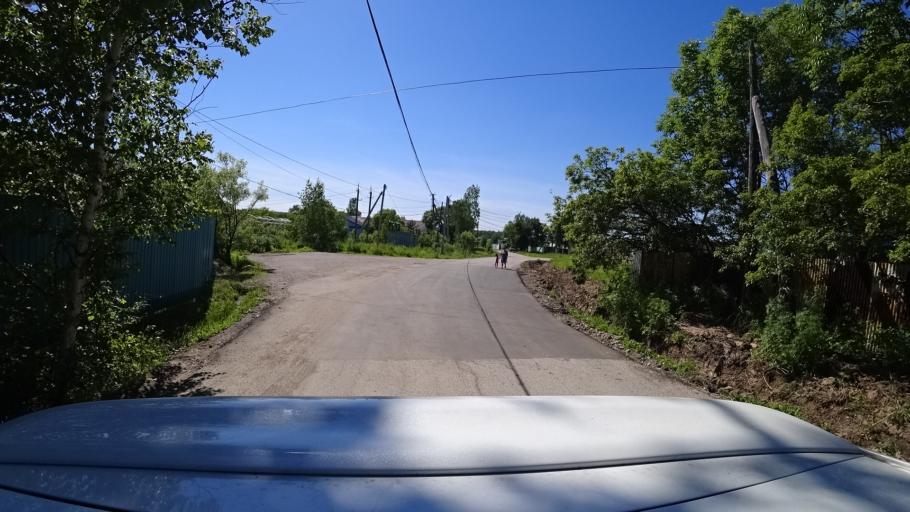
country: RU
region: Khabarovsk Krai
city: Topolevo
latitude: 48.5555
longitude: 135.1904
